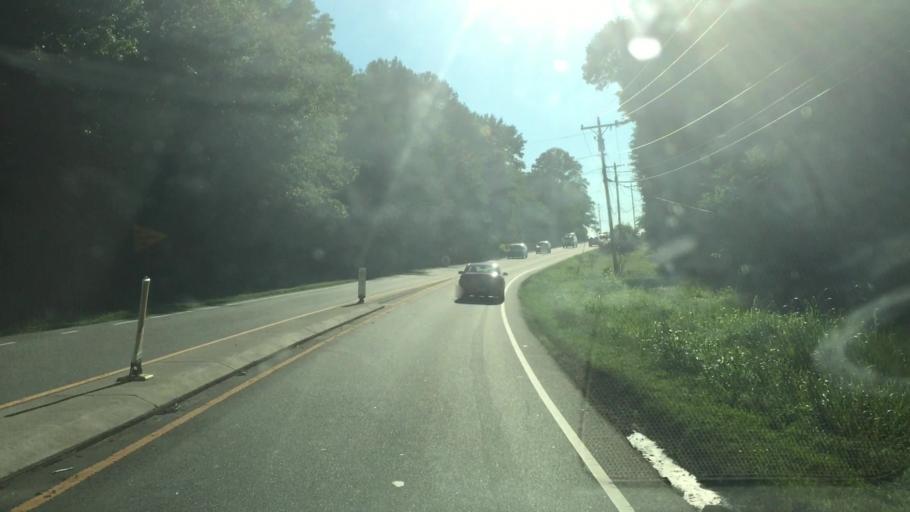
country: US
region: North Carolina
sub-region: Cabarrus County
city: Kannapolis
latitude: 35.4367
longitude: -80.6989
